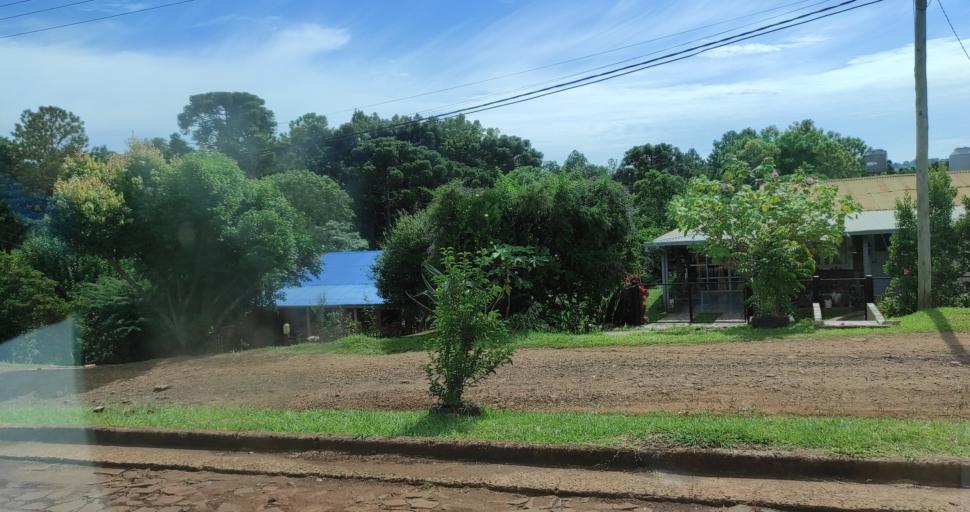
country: AR
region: Misiones
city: Dos de Mayo
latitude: -27.0373
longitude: -54.6846
